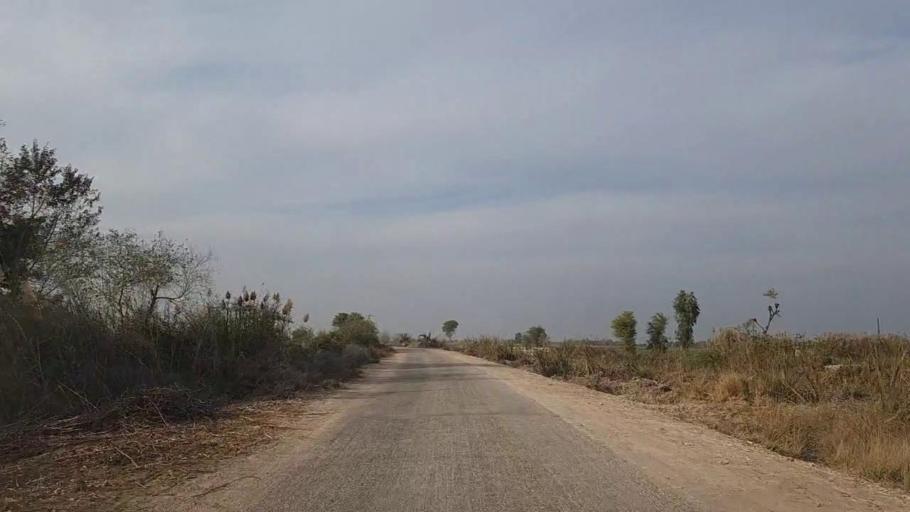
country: PK
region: Sindh
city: Daur
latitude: 26.4856
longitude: 68.4636
